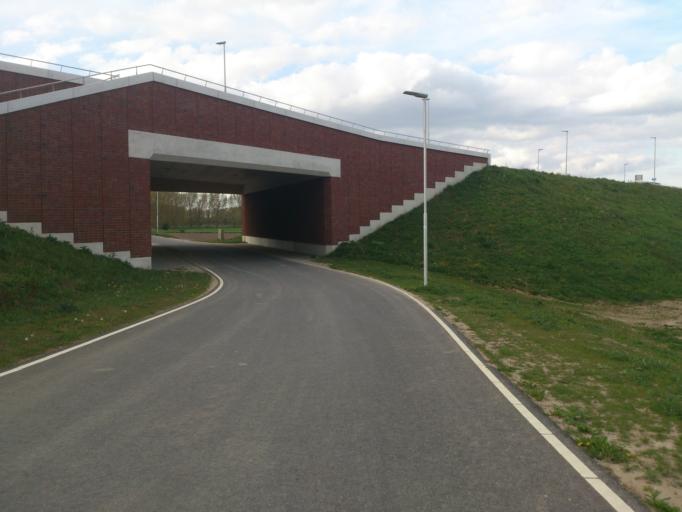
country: NL
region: Gelderland
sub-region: Gemeente Nijmegen
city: Nijmegen
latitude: 51.8643
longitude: 5.8473
